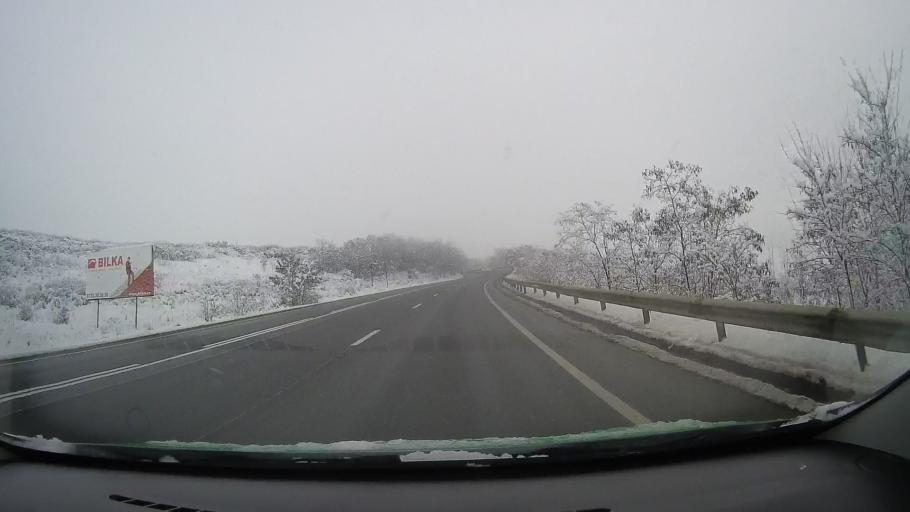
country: RO
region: Sibiu
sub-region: Comuna Cristian
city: Cristian
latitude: 45.7890
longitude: 24.0575
